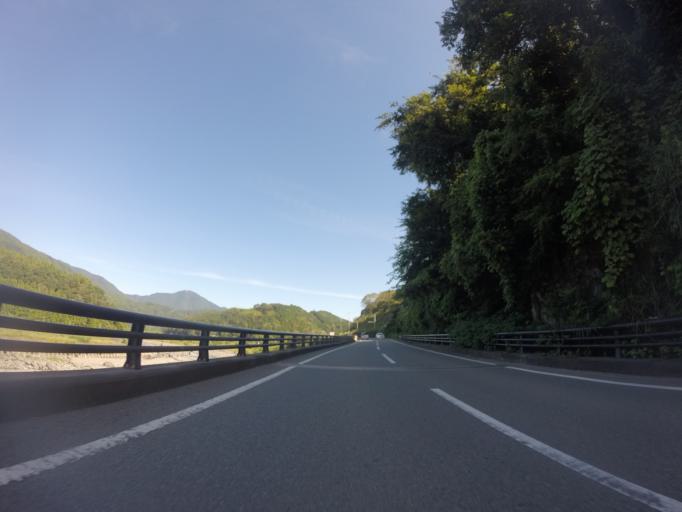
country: JP
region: Shizuoka
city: Fujinomiya
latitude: 35.3382
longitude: 138.4494
